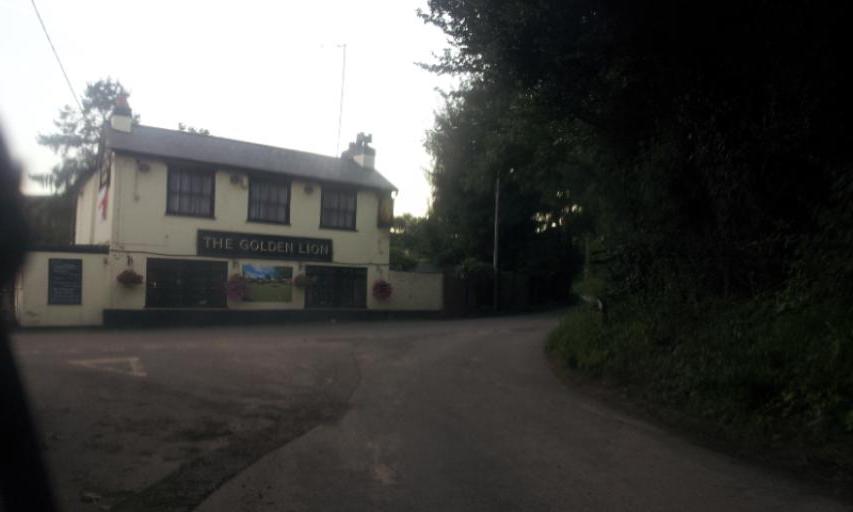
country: GB
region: England
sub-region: Kent
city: Meopham
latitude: 51.3749
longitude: 0.4014
